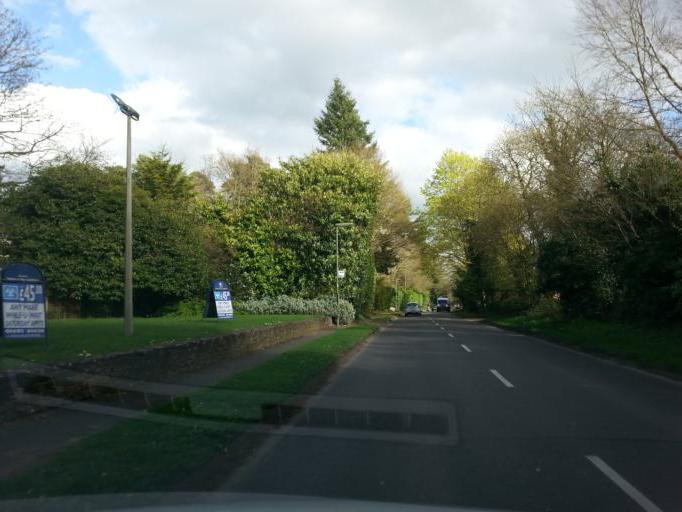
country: GB
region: England
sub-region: Surrey
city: Godalming
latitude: 51.2009
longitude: -0.6314
